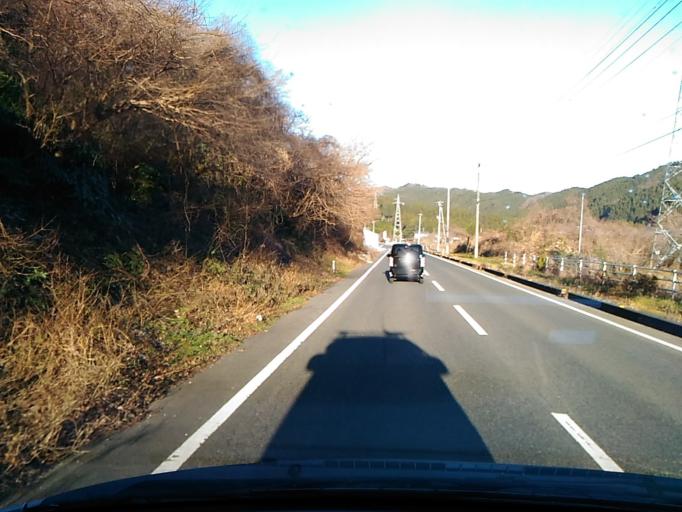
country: JP
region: Ibaraki
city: Kitaibaraki
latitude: 36.9227
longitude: 140.7013
